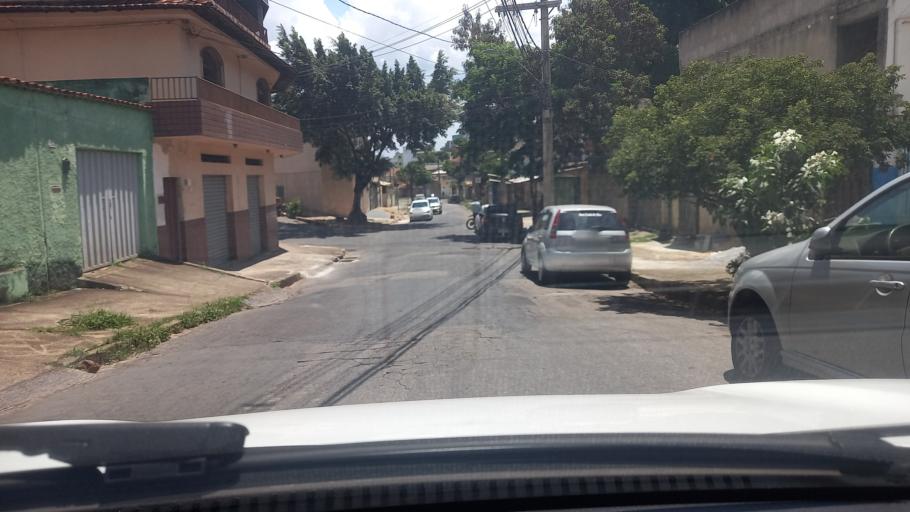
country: BR
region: Minas Gerais
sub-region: Belo Horizonte
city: Belo Horizonte
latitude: -19.9173
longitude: -43.9832
